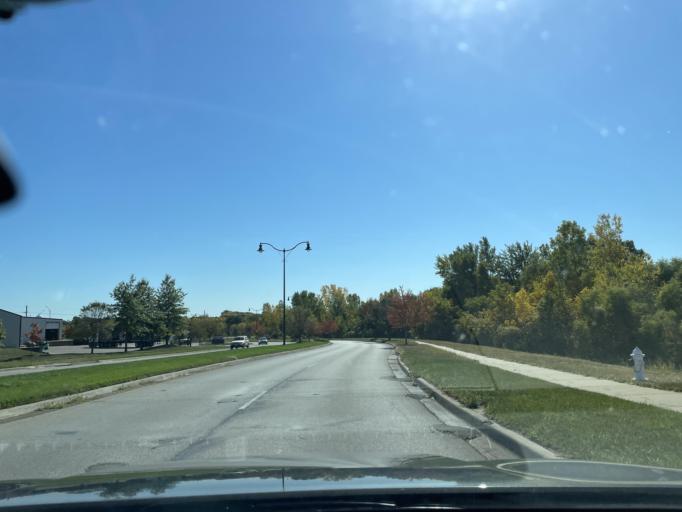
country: US
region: Missouri
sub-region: Andrew County
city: Country Club Village
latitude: 39.8144
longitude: -94.8075
